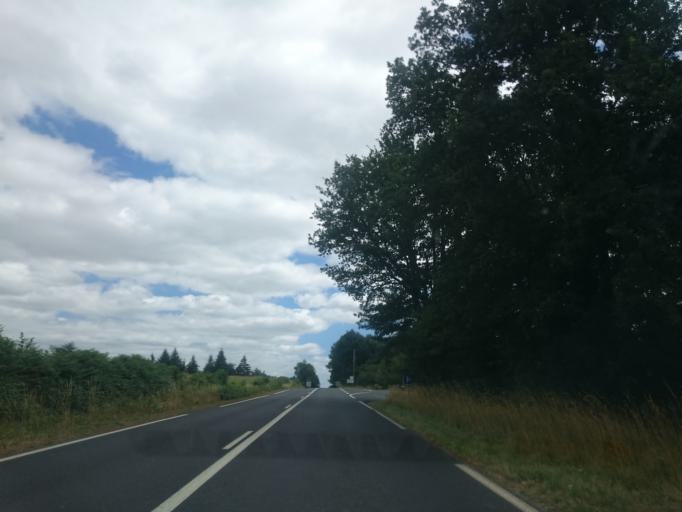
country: FR
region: Auvergne
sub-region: Departement du Cantal
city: Saint-Paul-des-Landes
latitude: 44.9567
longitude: 2.2750
